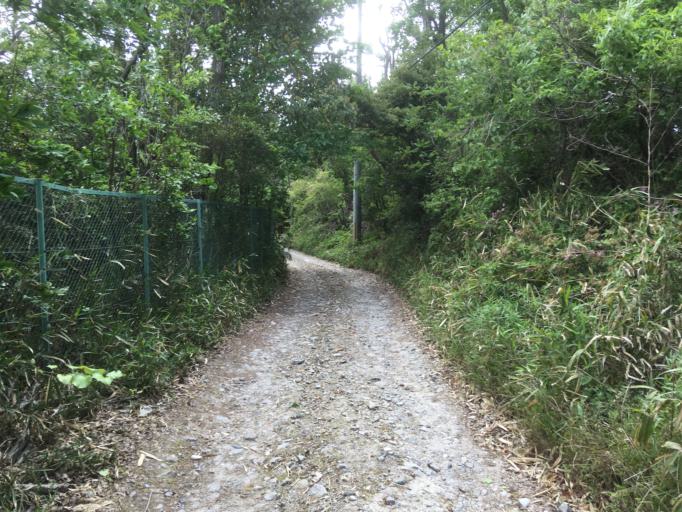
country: JP
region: Nara
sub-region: Ikoma-shi
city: Ikoma
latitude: 34.7047
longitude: 135.6790
